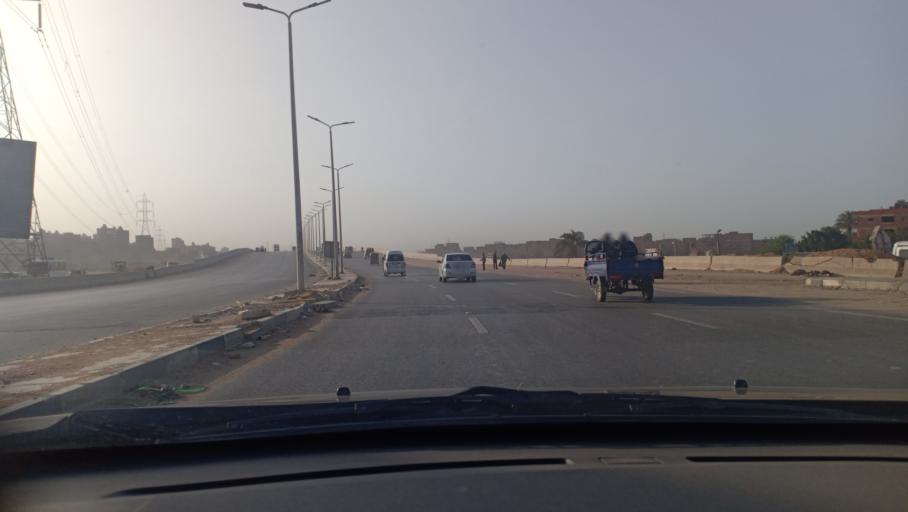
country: EG
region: Muhafazat al Qalyubiyah
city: Qalyub
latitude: 30.1415
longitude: 31.2637
